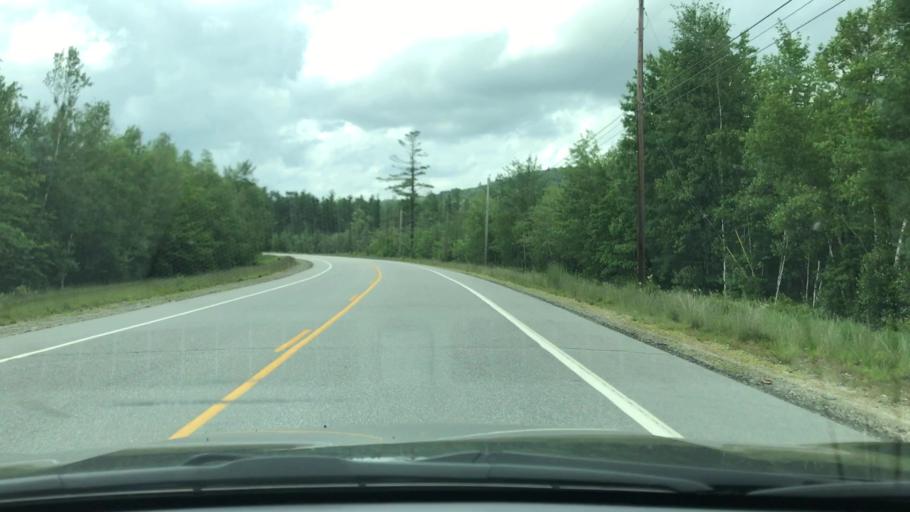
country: US
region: Maine
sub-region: Oxford County
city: Bethel
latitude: 44.4191
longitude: -70.7445
